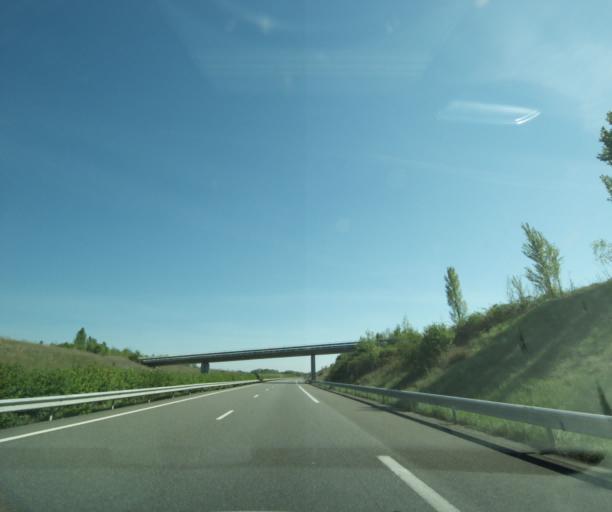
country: FR
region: Midi-Pyrenees
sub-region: Departement du Tarn-et-Garonne
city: Caussade
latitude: 44.2254
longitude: 1.5357
